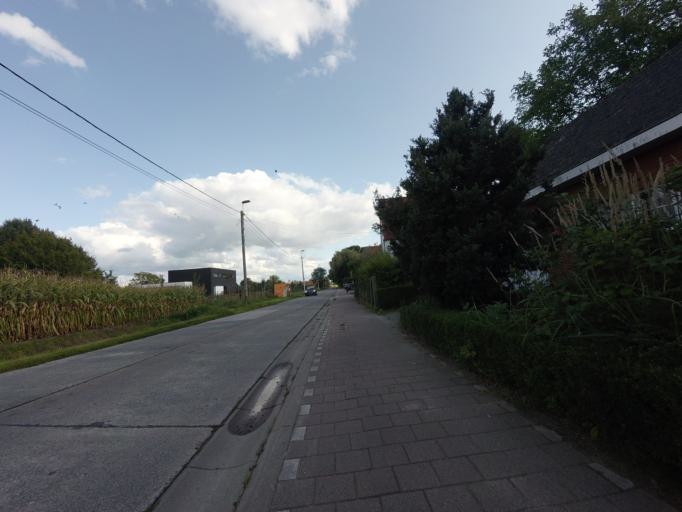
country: BE
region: Flanders
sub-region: Provincie Vlaams-Brabant
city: Londerzeel
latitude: 50.9847
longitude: 4.3248
